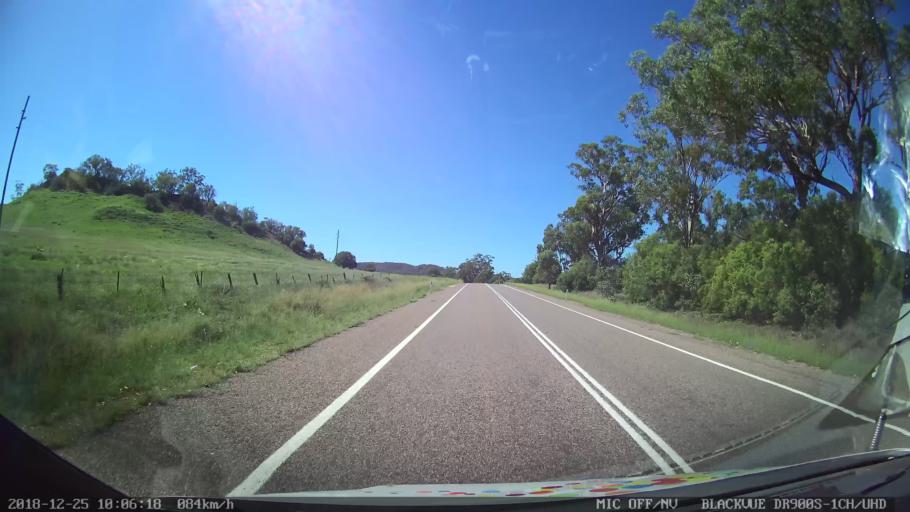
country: AU
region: New South Wales
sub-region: Upper Hunter Shire
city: Merriwa
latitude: -32.2584
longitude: 150.4893
